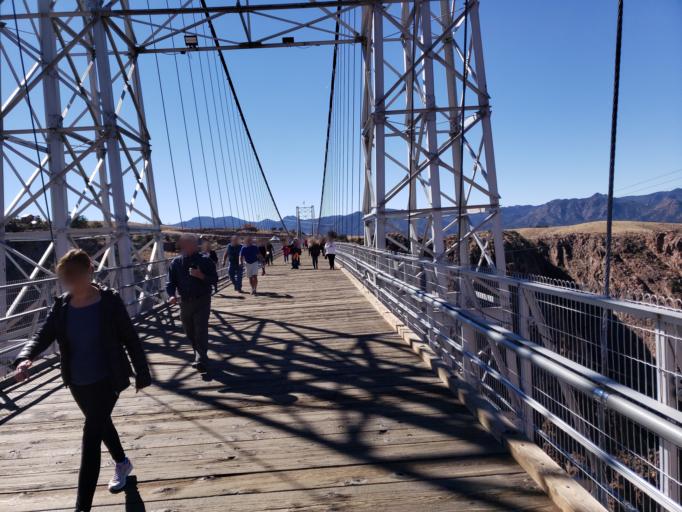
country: US
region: Colorado
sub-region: Fremont County
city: Canon City
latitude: 38.4622
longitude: -105.3243
